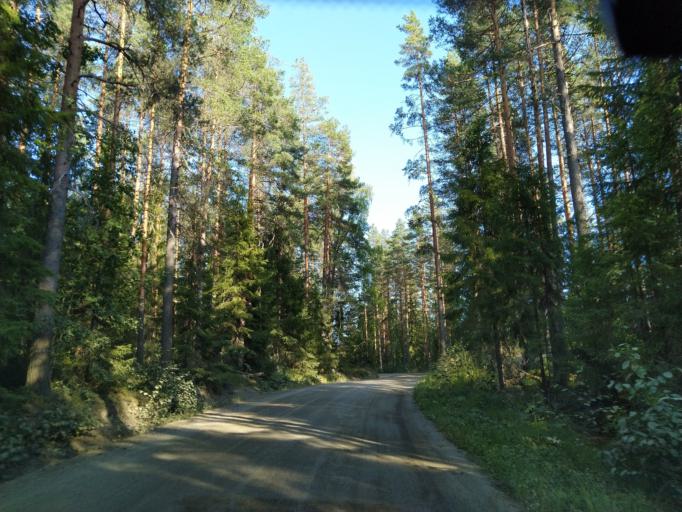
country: FI
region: Central Finland
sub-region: Jaemsae
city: Kuhmoinen
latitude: 61.6766
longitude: 24.9936
